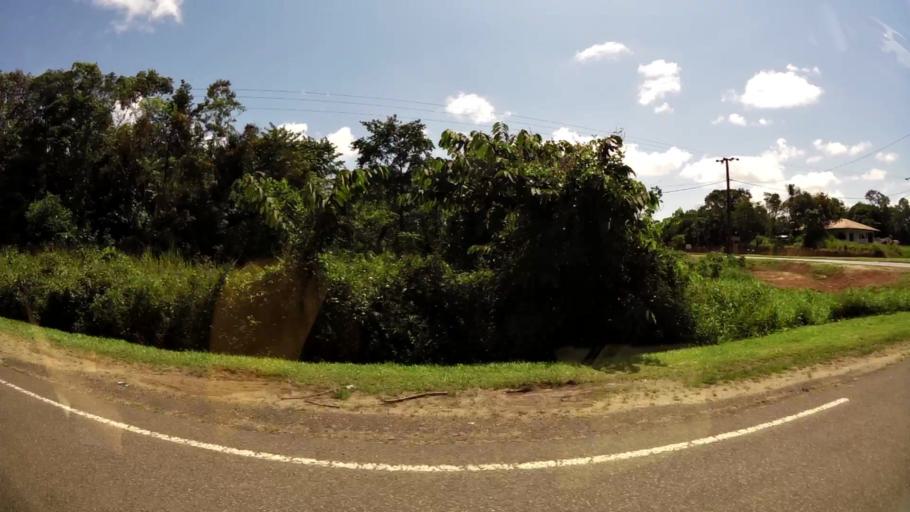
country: GF
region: Guyane
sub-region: Guyane
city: Matoury
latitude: 4.8349
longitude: -52.3251
